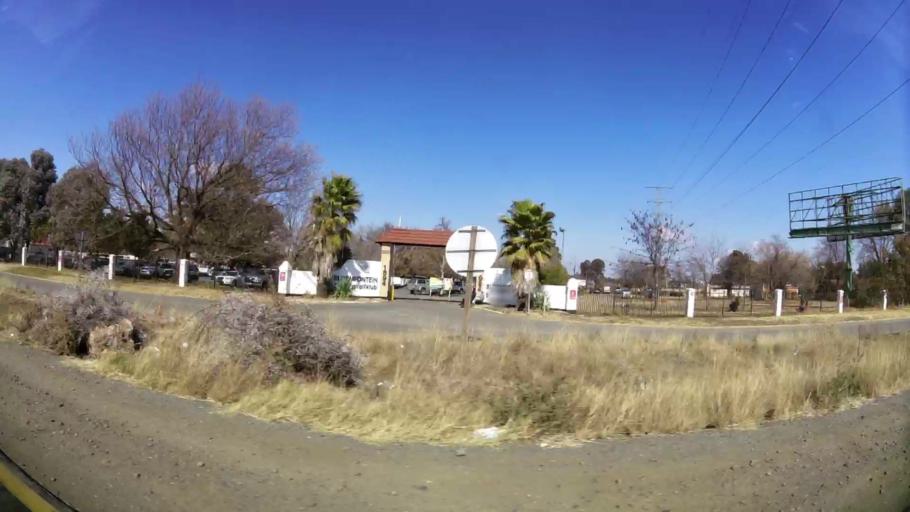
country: ZA
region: Orange Free State
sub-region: Mangaung Metropolitan Municipality
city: Bloemfontein
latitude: -29.1160
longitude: 26.2572
